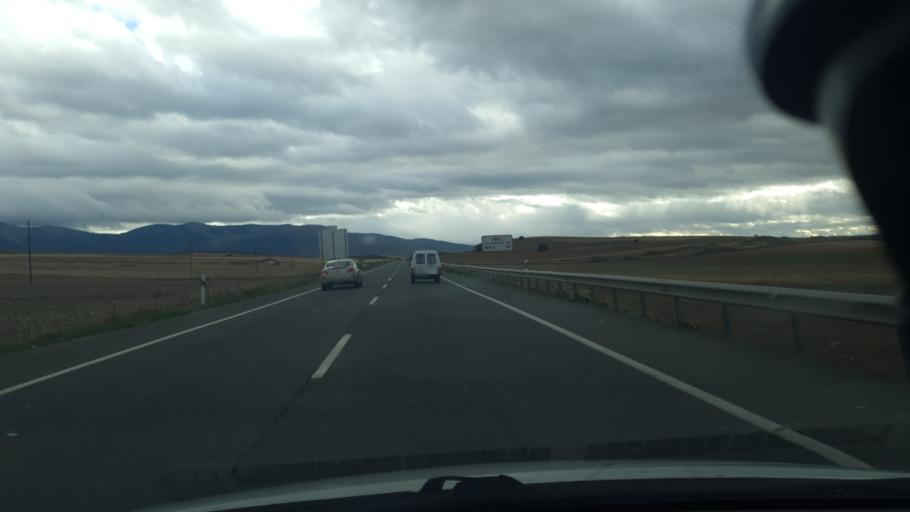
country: ES
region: Castille and Leon
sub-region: Provincia de Segovia
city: Segovia
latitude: 40.9152
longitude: -4.1581
